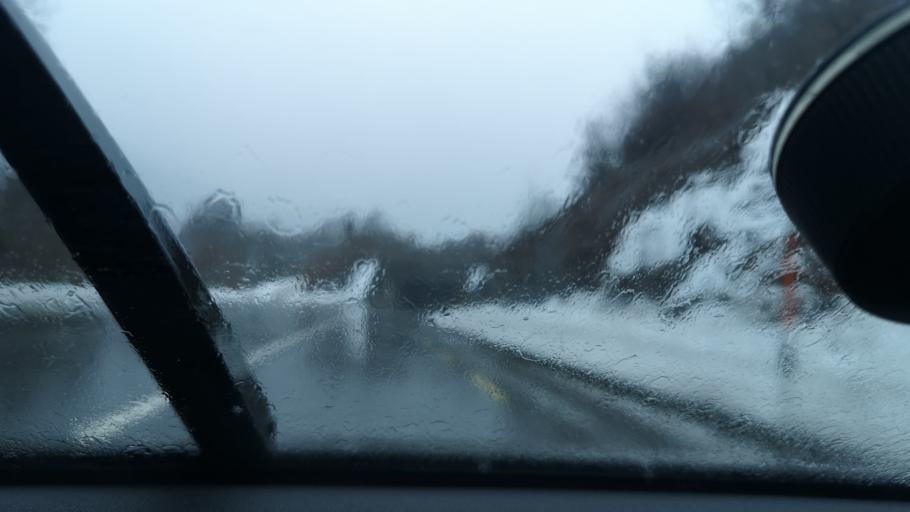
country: CH
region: Neuchatel
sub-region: Boudry District
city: Bevaix
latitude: 46.9660
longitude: 6.7786
